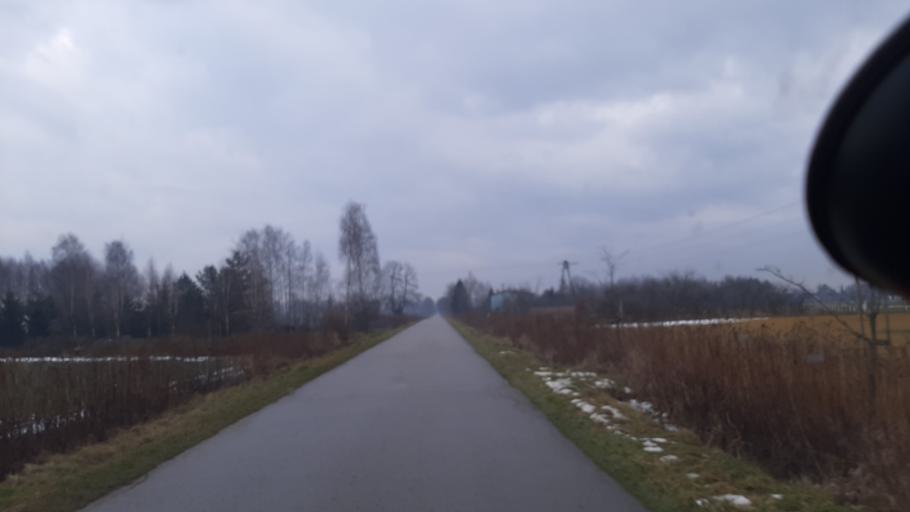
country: PL
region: Lublin Voivodeship
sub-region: Powiat lubelski
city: Lublin
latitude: 51.3380
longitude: 22.5422
